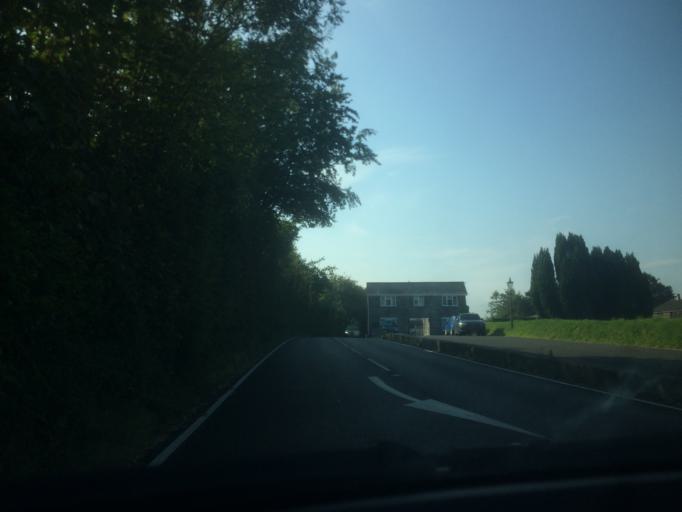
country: GB
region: England
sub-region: Cornwall
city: Pillaton
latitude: 50.4693
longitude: -4.2713
